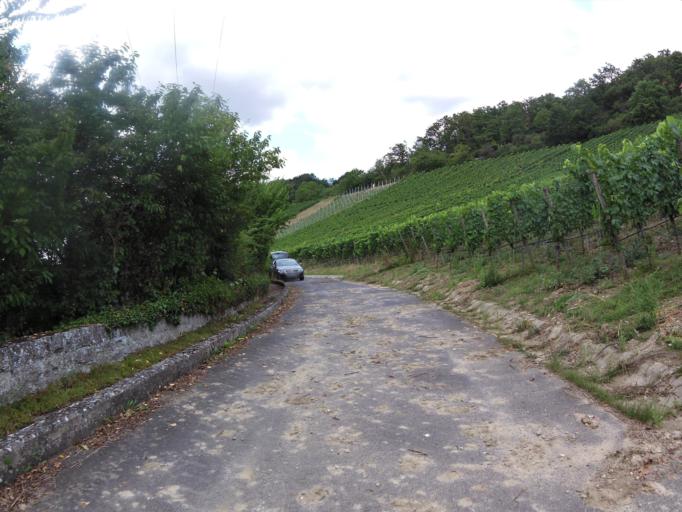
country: DE
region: Bavaria
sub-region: Regierungsbezirk Unterfranken
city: Sommerhausen
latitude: 49.7040
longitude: 10.0296
